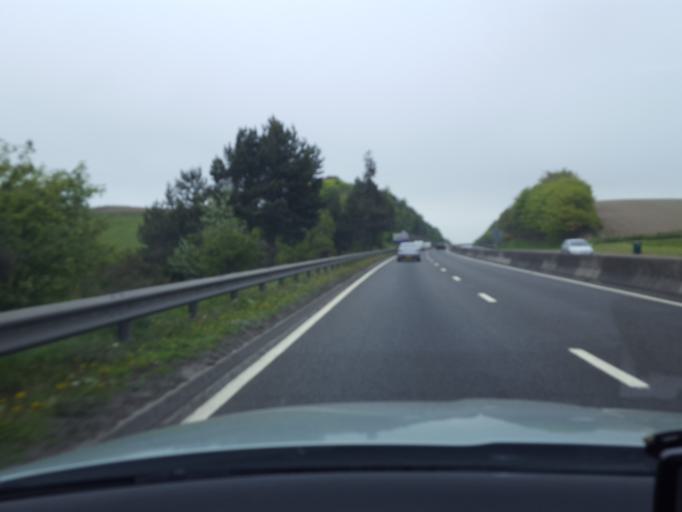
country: GB
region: Scotland
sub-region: Dundee City
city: Dundee
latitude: 56.4985
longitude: -2.9499
